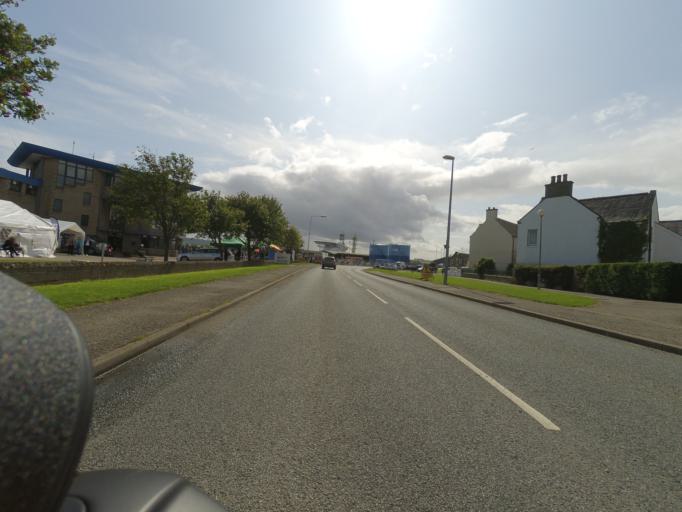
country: GB
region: Scotland
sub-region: Highland
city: Invergordon
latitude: 57.6872
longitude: -4.1672
